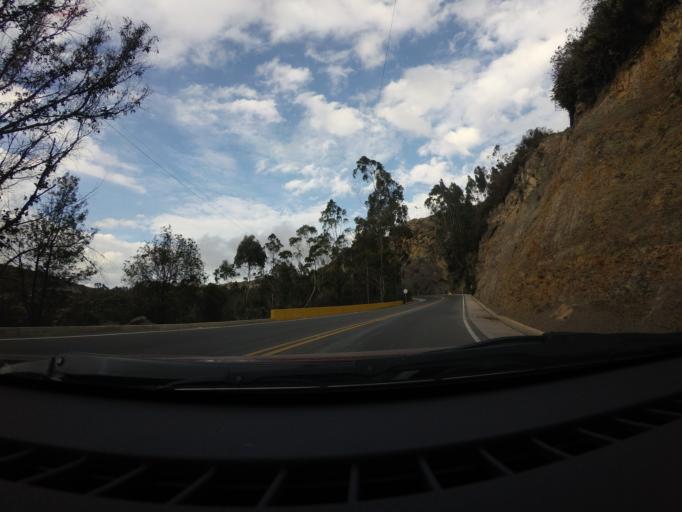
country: CO
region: Boyaca
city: Cucaita
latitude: 5.5614
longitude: -73.4303
